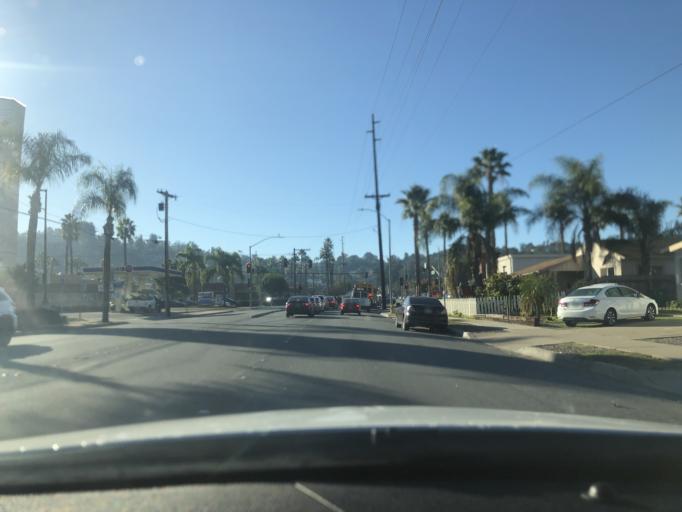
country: US
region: California
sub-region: San Diego County
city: El Cajon
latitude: 32.7814
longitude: -116.9579
